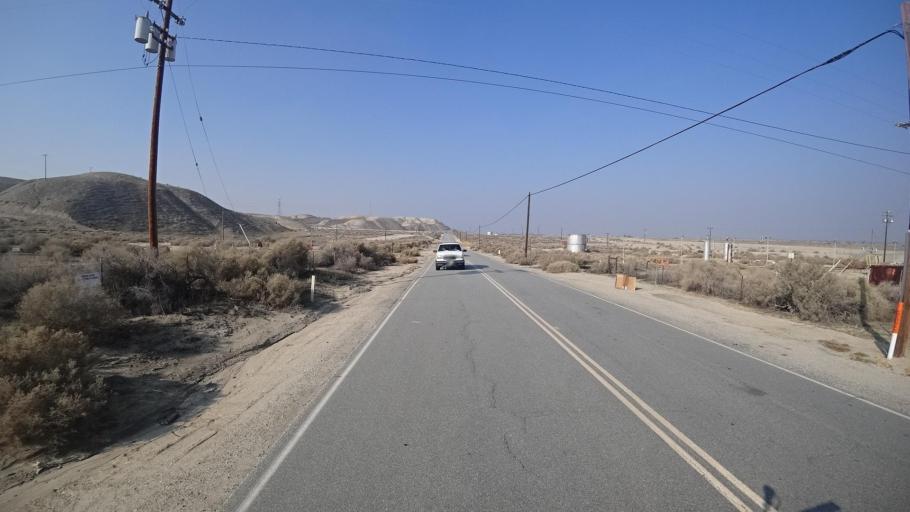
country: US
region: California
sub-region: Kern County
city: Ford City
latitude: 35.2758
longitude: -119.3219
